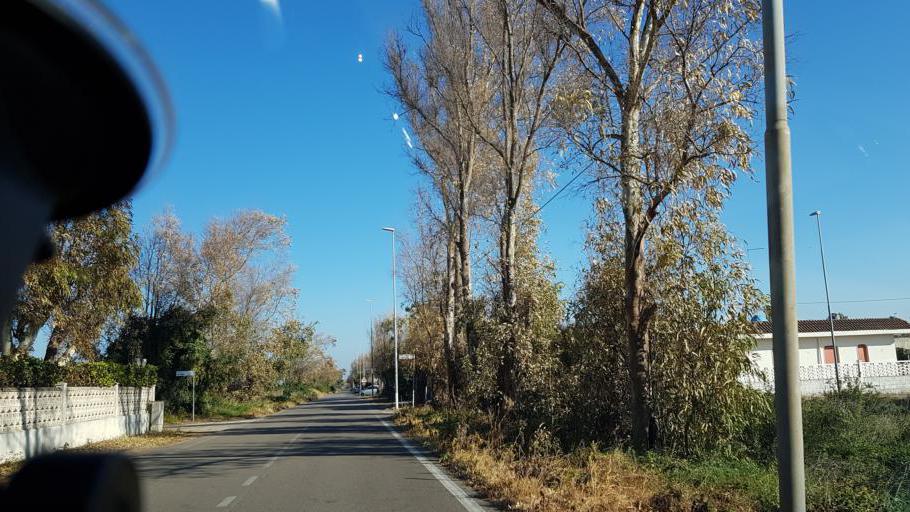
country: IT
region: Apulia
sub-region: Provincia di Lecce
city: Giorgilorio
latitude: 40.4539
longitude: 18.2161
